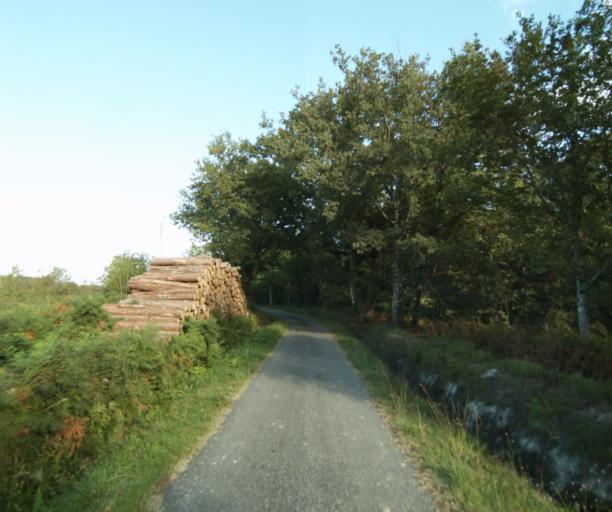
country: FR
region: Midi-Pyrenees
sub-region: Departement du Gers
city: Cazaubon
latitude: 43.8955
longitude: -0.0035
